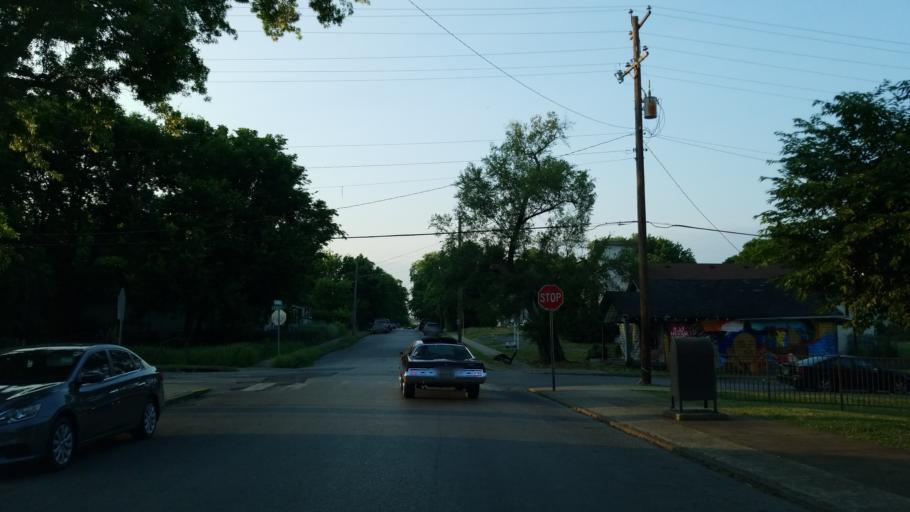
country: US
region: Tennessee
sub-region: Davidson County
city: Nashville
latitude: 36.1506
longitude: -86.7609
